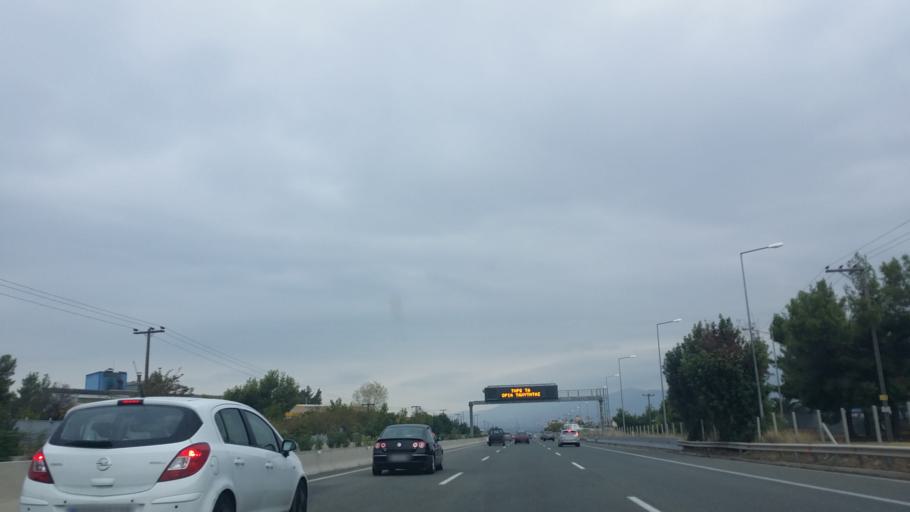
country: GR
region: Central Greece
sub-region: Nomos Voiotias
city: Oinofyta
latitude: 38.3170
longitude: 23.6280
